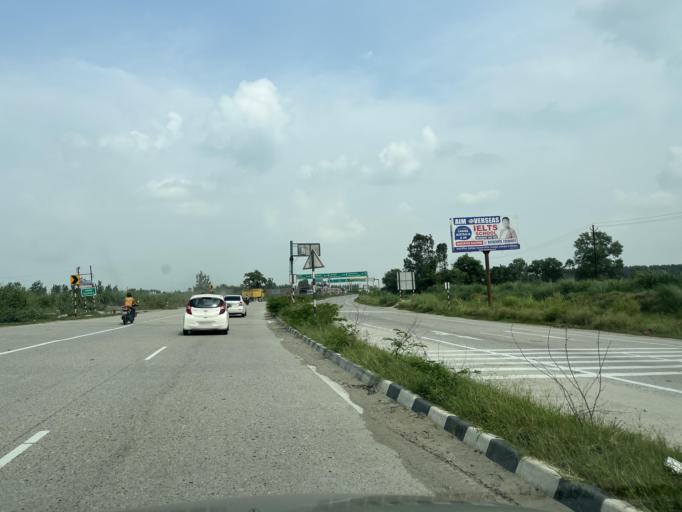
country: IN
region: Uttarakhand
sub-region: Udham Singh Nagar
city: Bazpur
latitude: 29.1499
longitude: 79.0839
